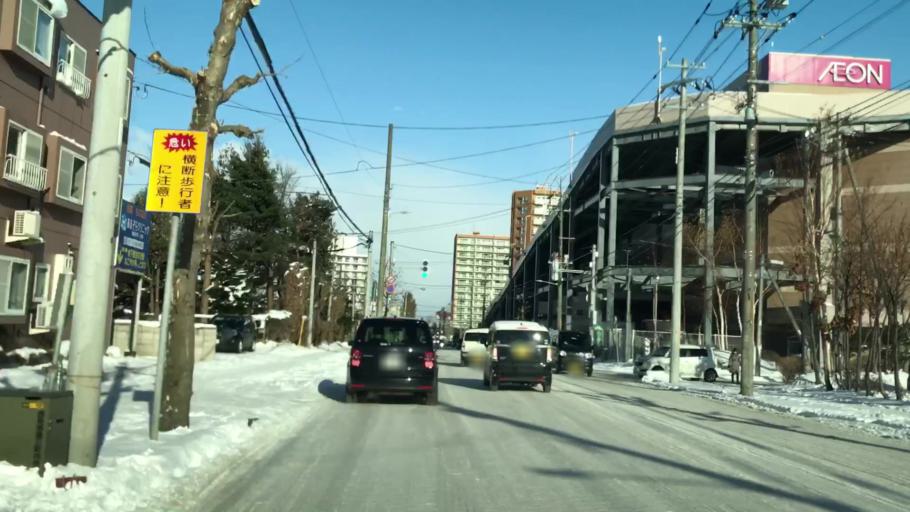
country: JP
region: Hokkaido
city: Sapporo
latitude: 43.0962
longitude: 141.2749
